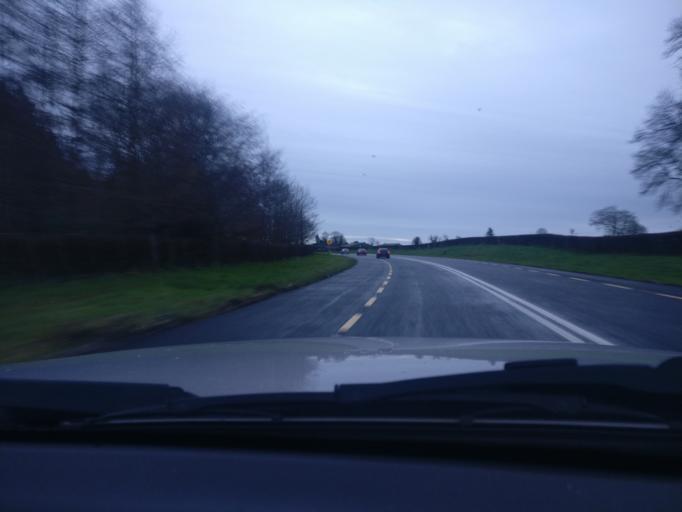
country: IE
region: Leinster
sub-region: An Mhi
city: Kells
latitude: 53.6938
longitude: -6.7863
